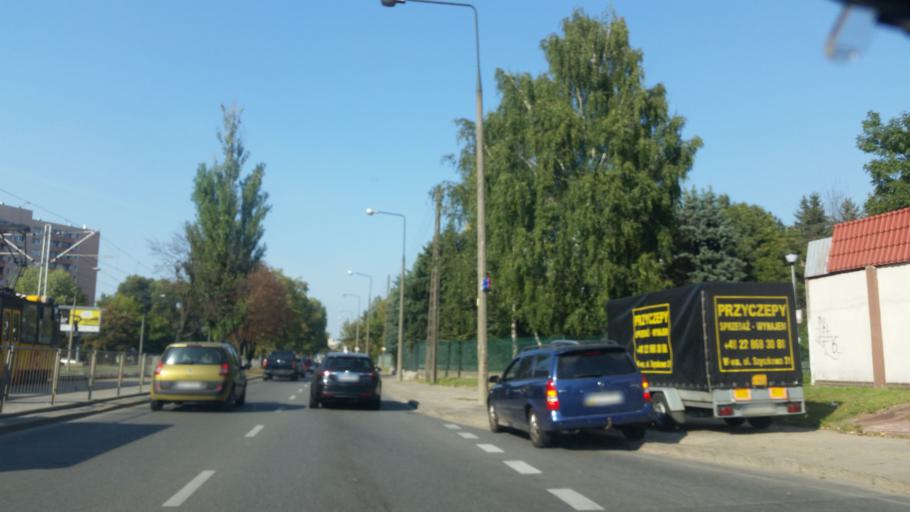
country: PL
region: Masovian Voivodeship
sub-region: Warszawa
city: Bemowo
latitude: 52.2257
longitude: 20.9165
